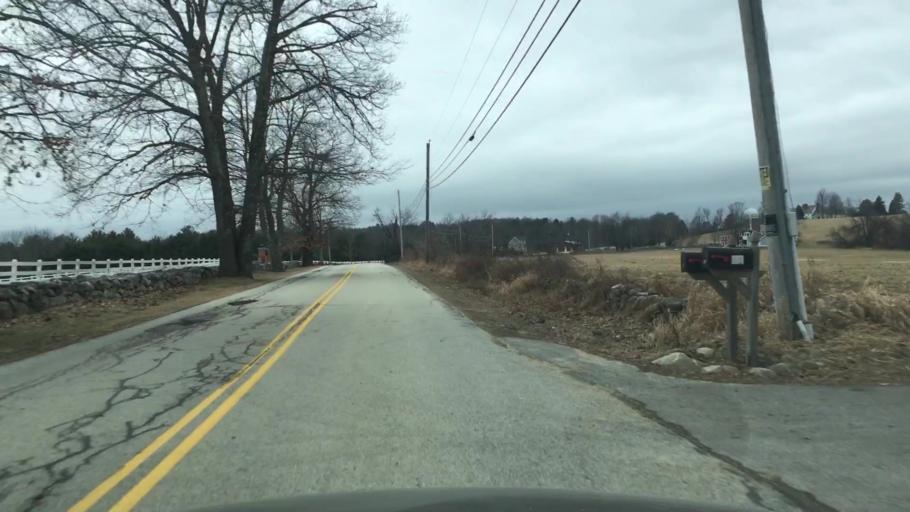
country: US
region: New Hampshire
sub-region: Hillsborough County
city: Mont Vernon
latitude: 42.9278
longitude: -71.6067
